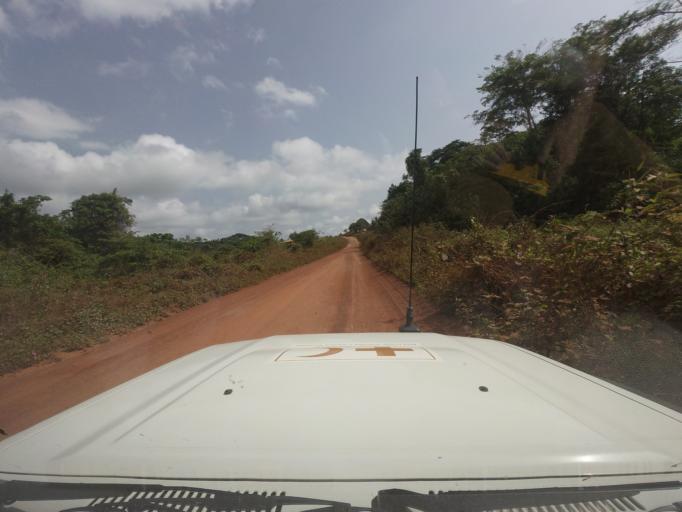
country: LR
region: Bong
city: Gbarnga
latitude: 7.2150
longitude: -9.4394
